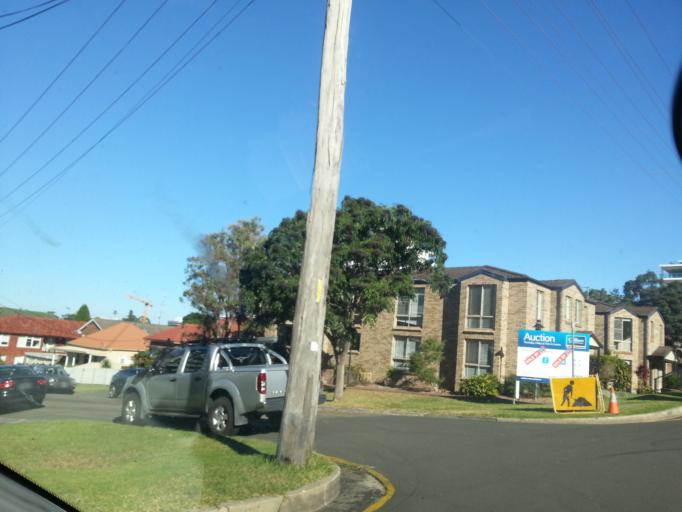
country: AU
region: New South Wales
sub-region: Wollongong
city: Wollongong
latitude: -34.4187
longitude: 150.9002
